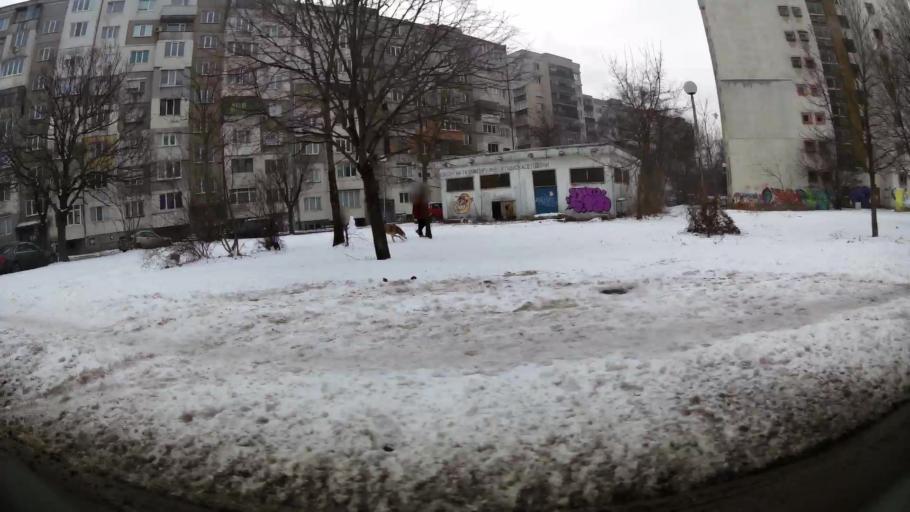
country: BG
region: Sofia-Capital
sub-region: Stolichna Obshtina
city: Sofia
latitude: 42.7130
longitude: 23.2938
